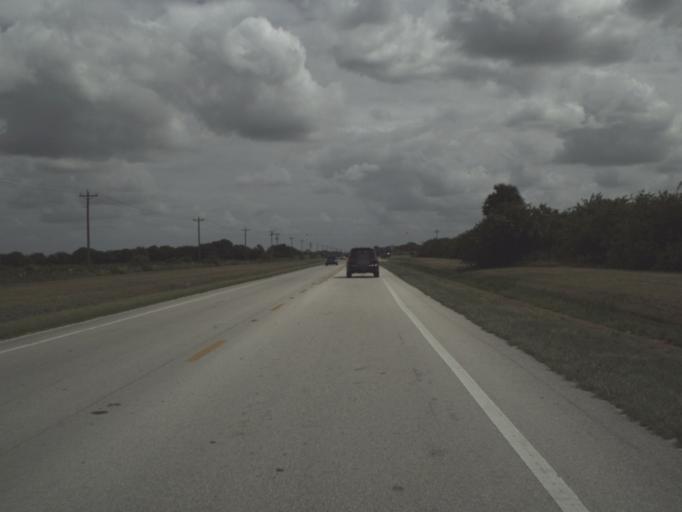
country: US
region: Florida
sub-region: Collier County
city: Immokalee
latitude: 26.4906
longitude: -81.4545
